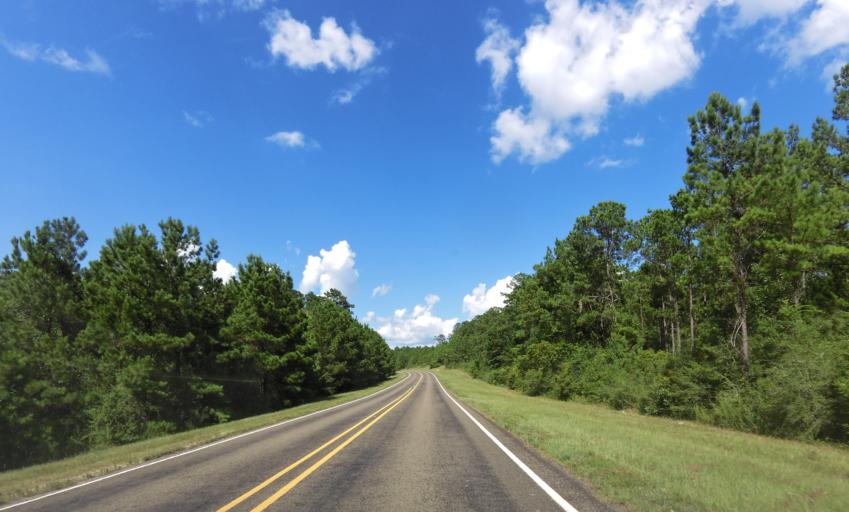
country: US
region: Texas
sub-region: Sabine County
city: Hemphill
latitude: 31.1504
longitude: -93.5977
